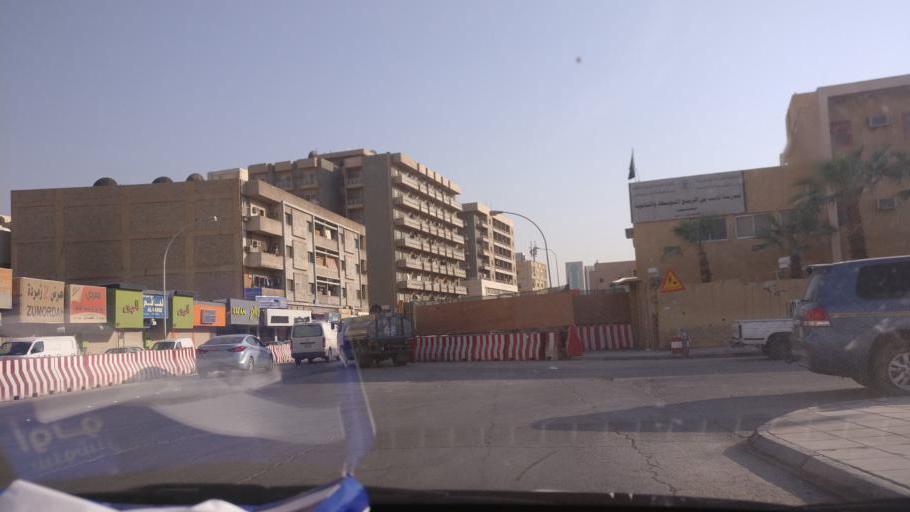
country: SA
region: Ar Riyad
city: Riyadh
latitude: 24.6404
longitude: 46.7147
